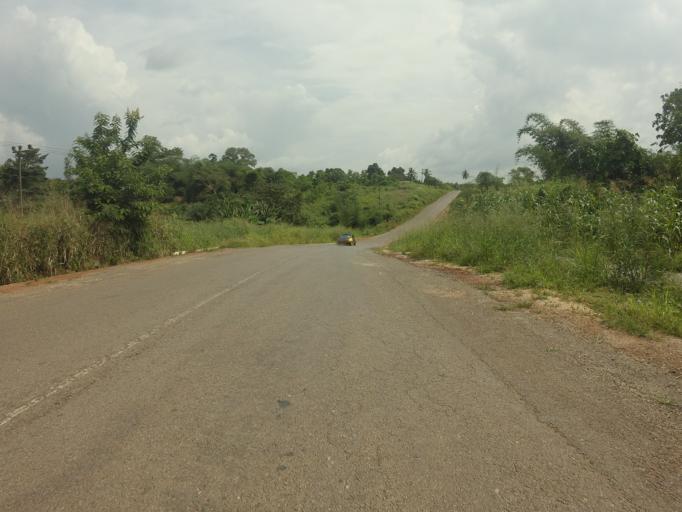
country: GH
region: Eastern
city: Aburi
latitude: 5.9594
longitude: -0.2166
